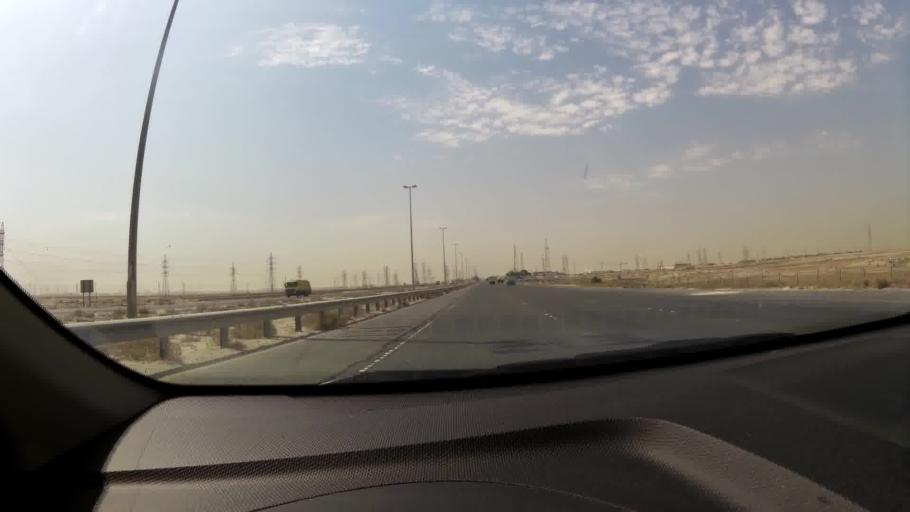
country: SA
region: Eastern Province
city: Al Khafji
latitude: 28.7405
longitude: 48.2840
